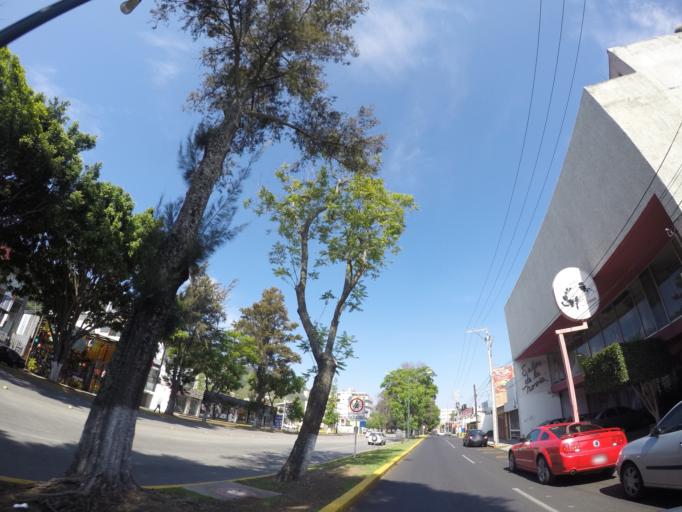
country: MX
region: Michoacan
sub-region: Morelia
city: Montana Monarca (Punta Altozano)
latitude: 19.6822
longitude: -101.1702
